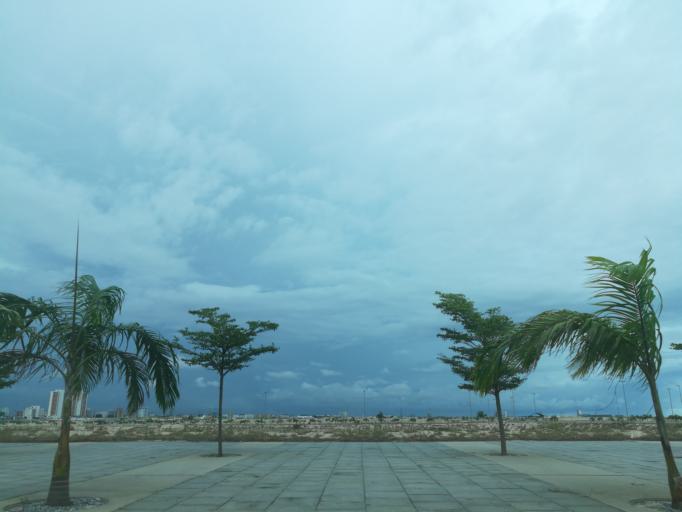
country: NG
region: Lagos
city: Ikoyi
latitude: 6.4099
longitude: 3.4178
